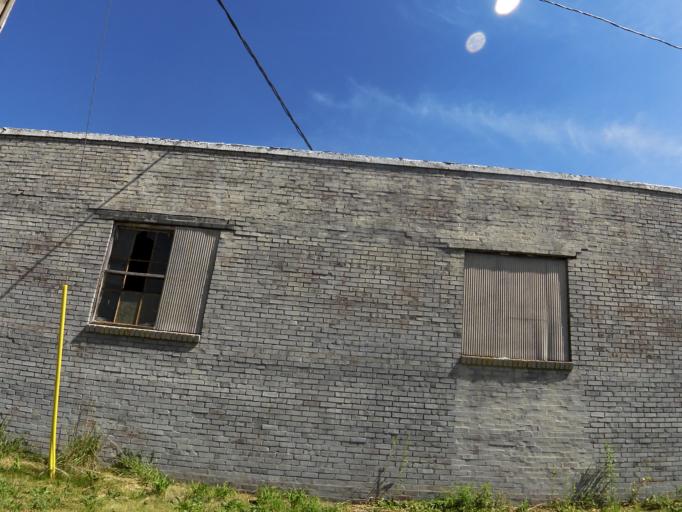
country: US
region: Illinois
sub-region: Vermilion County
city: Danville
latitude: 40.1362
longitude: -87.5974
